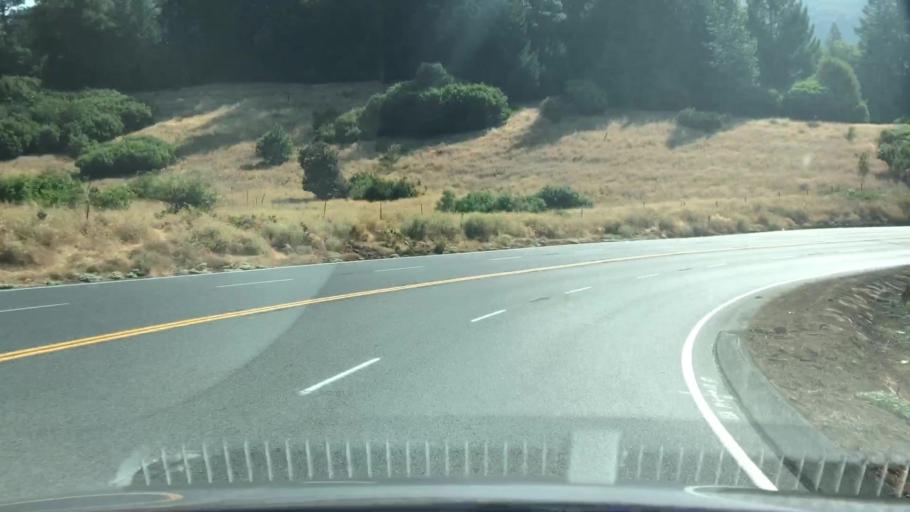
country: US
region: California
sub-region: Napa County
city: Calistoga
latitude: 38.6497
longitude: -122.5951
